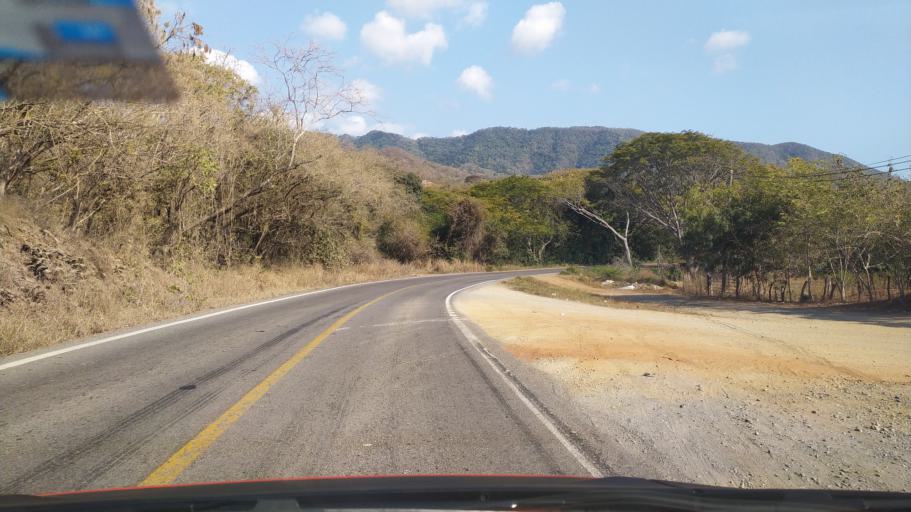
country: MX
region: Michoacan
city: Coahuayana Viejo
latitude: 18.5940
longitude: -103.6732
